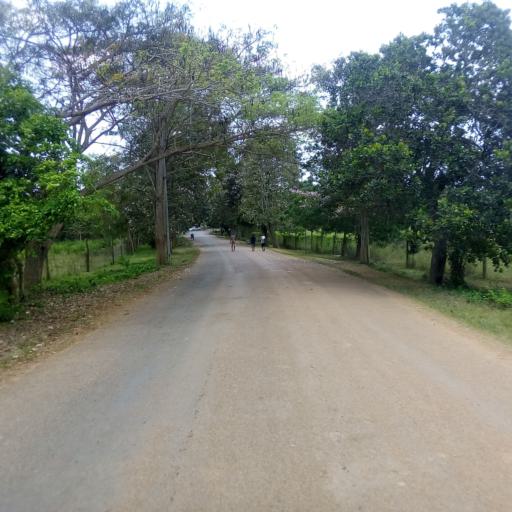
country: GH
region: Central
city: Cape Coast
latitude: 5.1318
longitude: -1.2912
